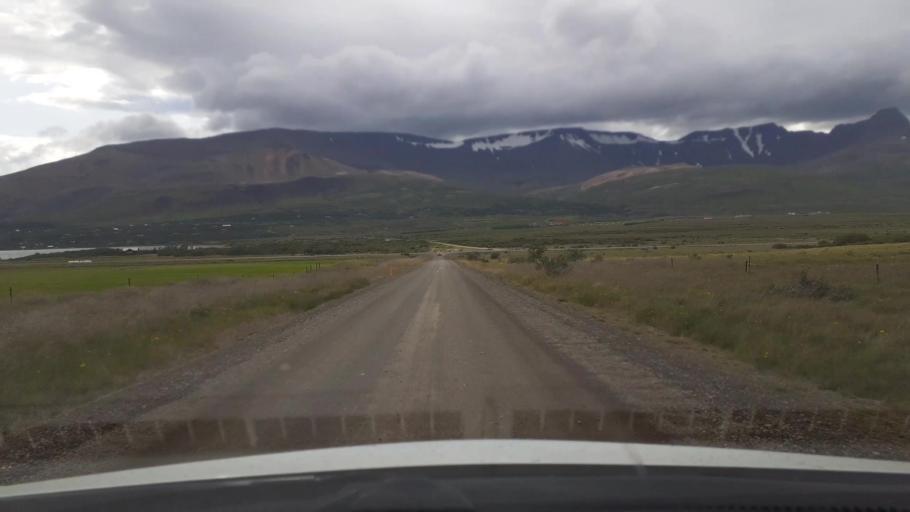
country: IS
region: West
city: Borgarnes
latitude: 64.5461
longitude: -21.6194
